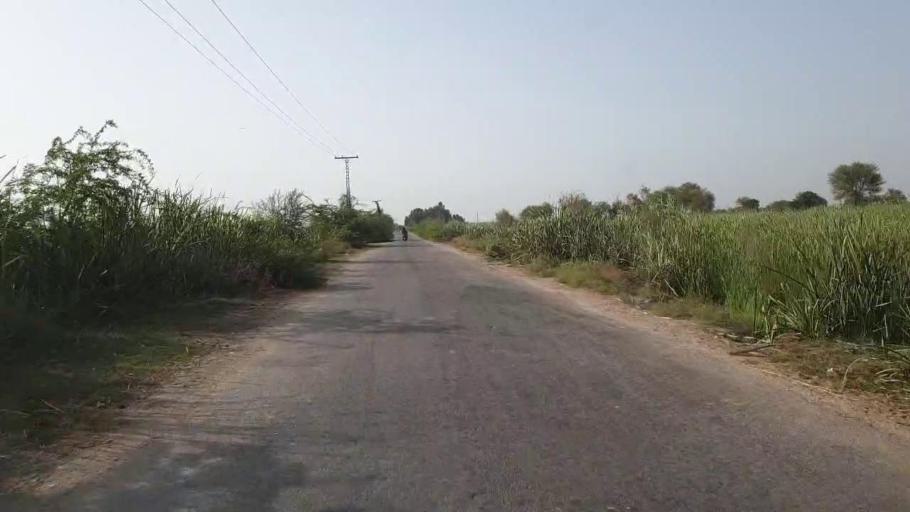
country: PK
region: Sindh
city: Jam Sahib
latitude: 26.4032
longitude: 68.8776
